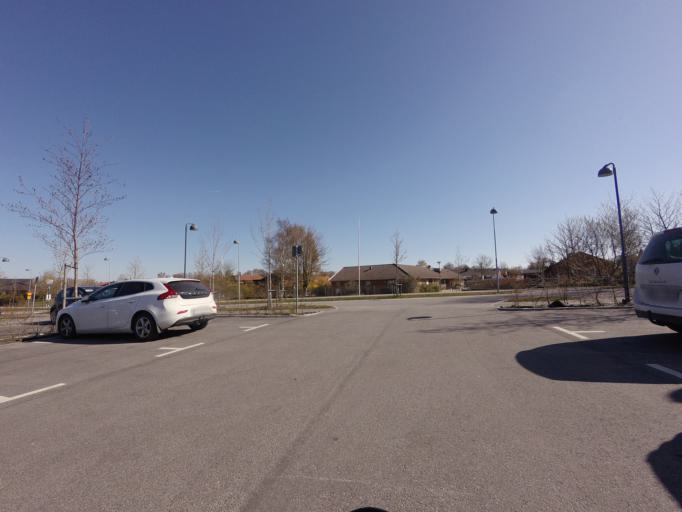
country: SE
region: Skane
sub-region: Malmo
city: Oxie
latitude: 55.4900
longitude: 13.1088
